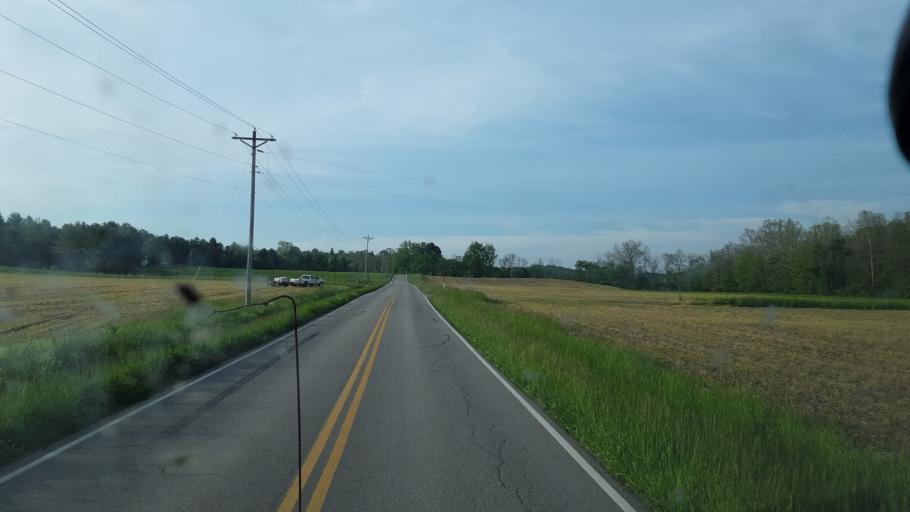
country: US
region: Ohio
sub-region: Ross County
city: Kingston
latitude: 39.5051
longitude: -82.6994
